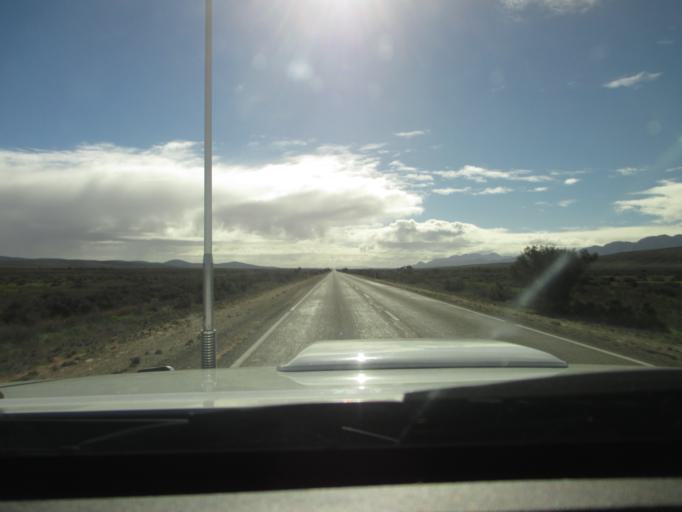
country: AU
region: South Australia
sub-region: Flinders Ranges
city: Quorn
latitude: -31.7265
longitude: 138.3450
